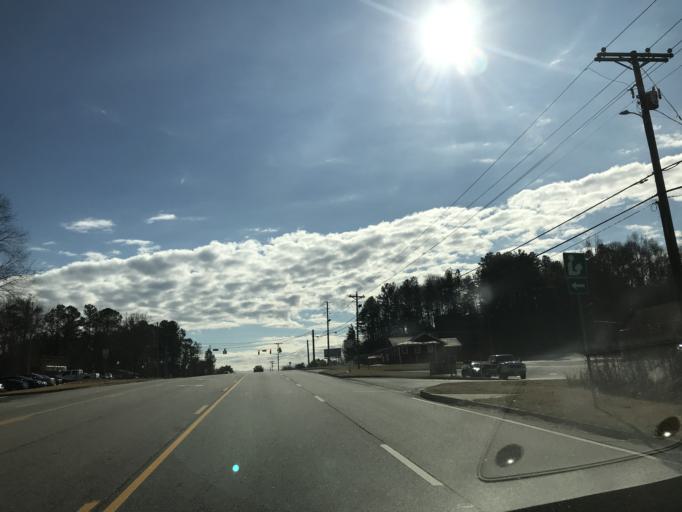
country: US
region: Georgia
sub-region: Paulding County
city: Hiram
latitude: 33.8668
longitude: -84.7638
